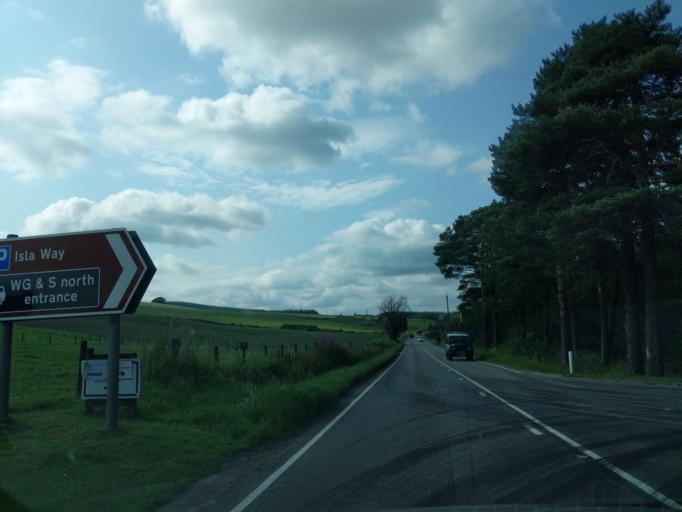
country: GB
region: Scotland
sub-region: Moray
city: Dufftown
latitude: 57.4597
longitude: -3.1325
